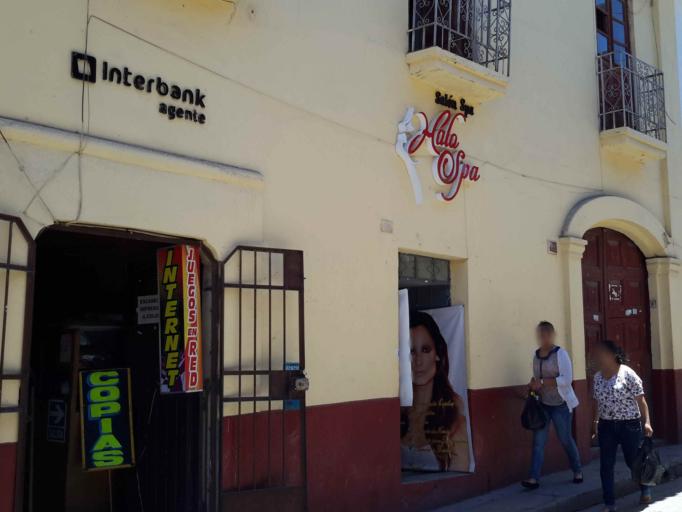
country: PE
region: Ayacucho
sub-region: Provincia de Huamanga
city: Ayacucho
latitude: -13.1638
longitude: -74.2254
